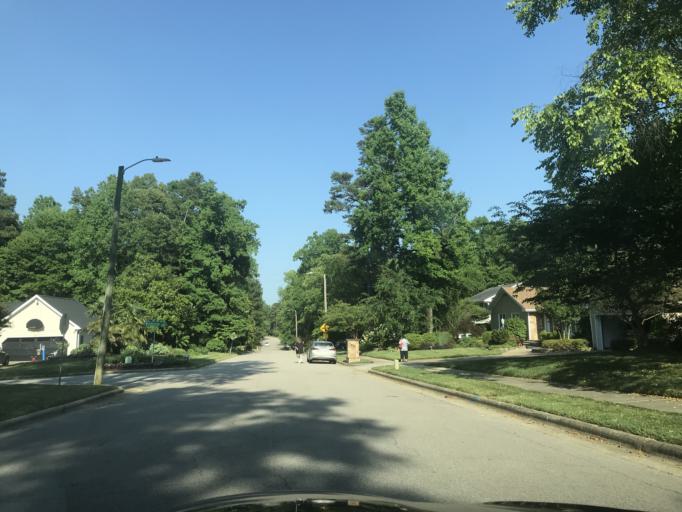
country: US
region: North Carolina
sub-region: Wake County
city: West Raleigh
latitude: 35.8719
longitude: -78.6143
